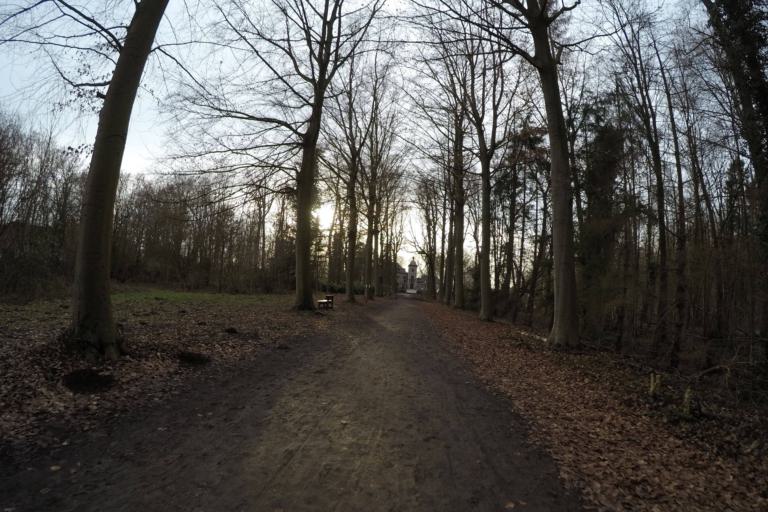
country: BE
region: Flanders
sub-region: Provincie Antwerpen
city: Ranst
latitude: 51.1956
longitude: 4.5598
